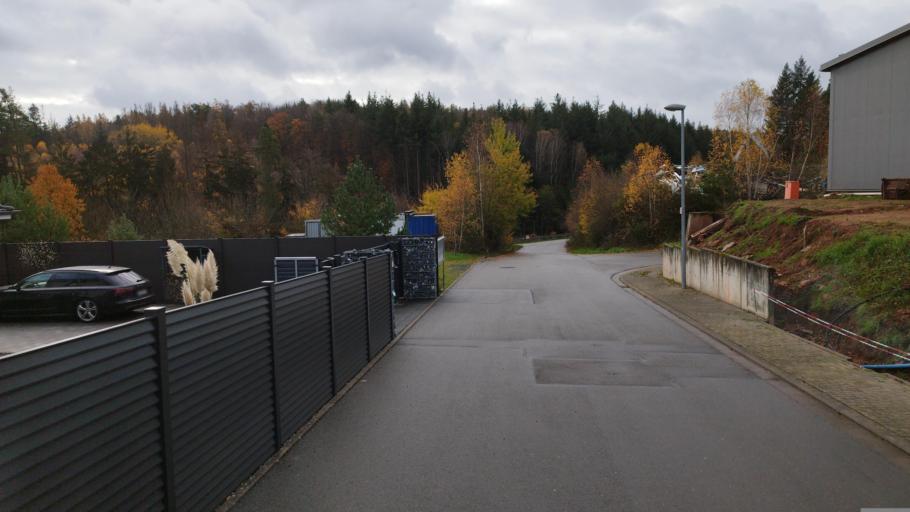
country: DE
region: Rheinland-Pfalz
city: Hochspeyer
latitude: 49.4409
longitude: 7.8721
